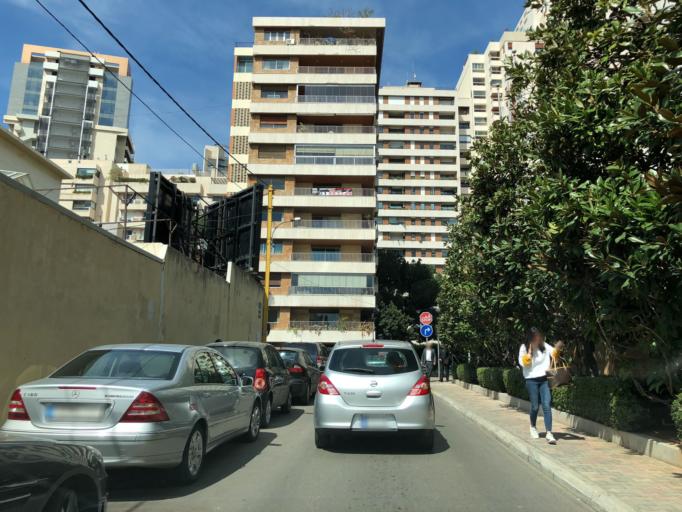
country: LB
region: Beyrouth
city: Beirut
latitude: 33.8864
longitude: 35.5165
